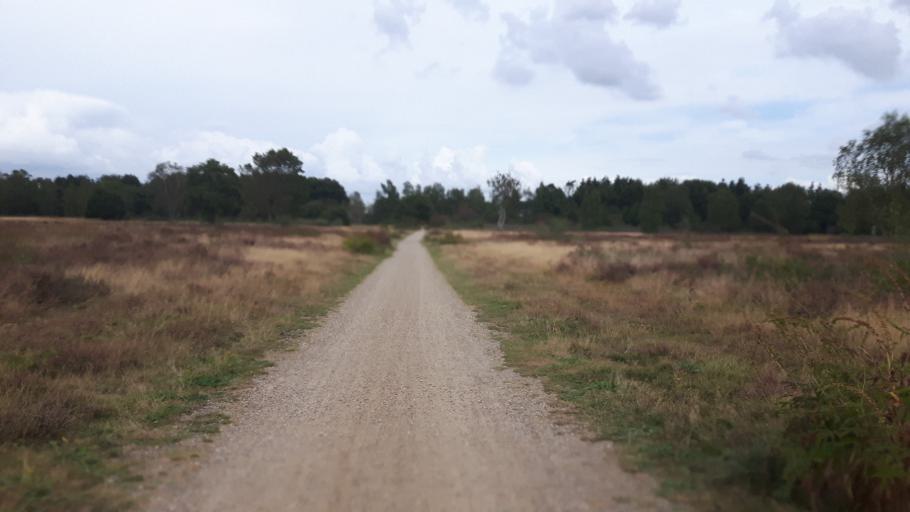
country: NL
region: Gelderland
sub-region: Gemeente Ermelo
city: Ermelo
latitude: 52.2866
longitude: 5.6080
